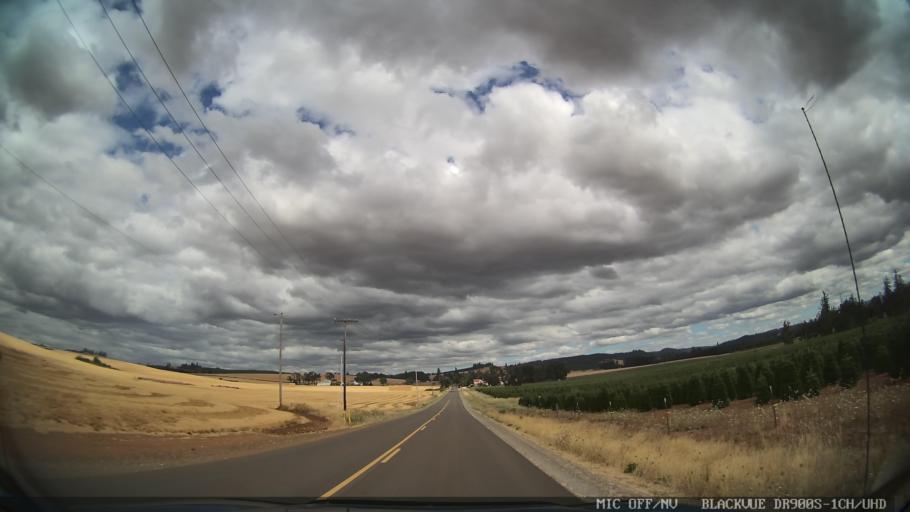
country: US
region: Oregon
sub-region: Marion County
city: Sublimity
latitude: 44.8661
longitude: -122.7645
